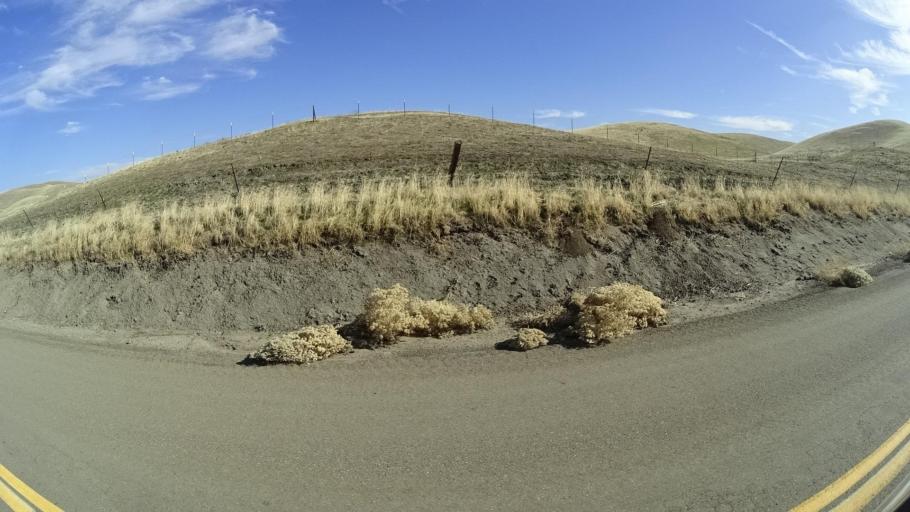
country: US
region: California
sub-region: Kern County
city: Oildale
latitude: 35.6222
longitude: -118.9409
